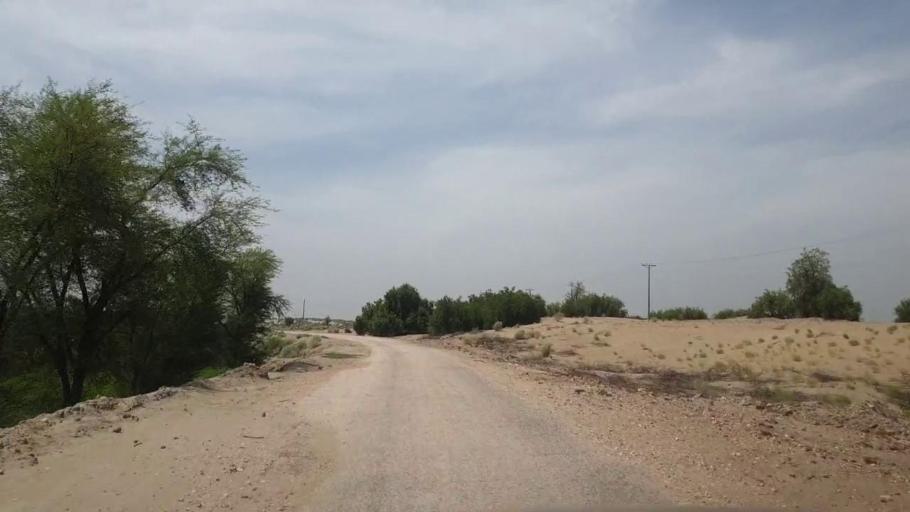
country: PK
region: Sindh
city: Kot Diji
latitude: 27.0884
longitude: 69.0743
